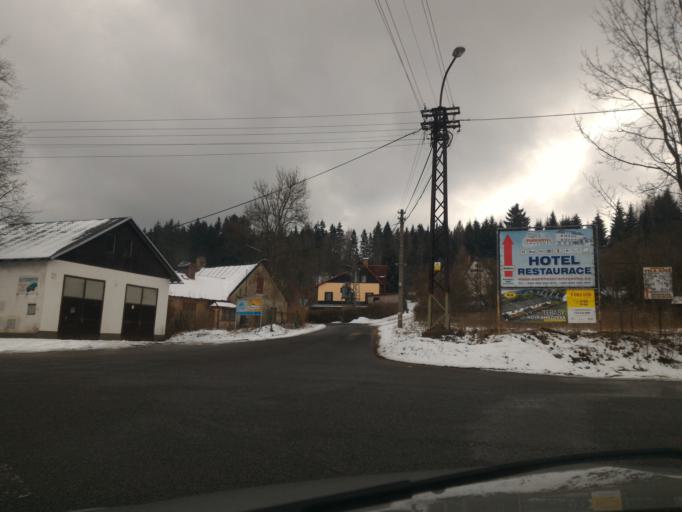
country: CZ
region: Liberecky
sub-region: Okres Jablonec nad Nisou
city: Lucany nad Nisou
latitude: 50.7384
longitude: 15.2304
